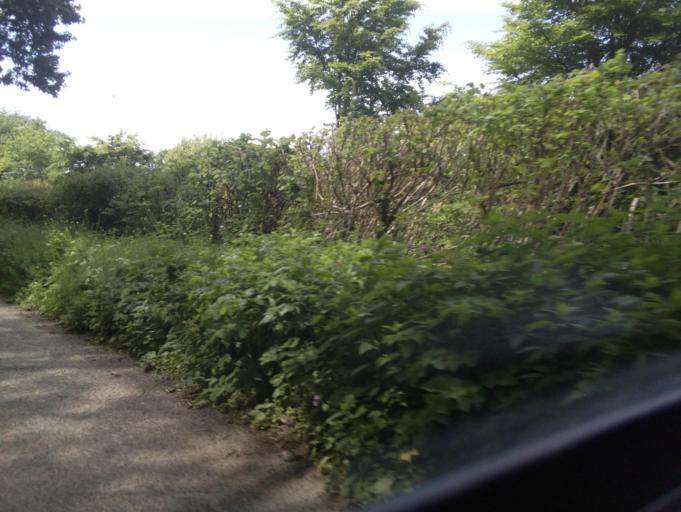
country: GB
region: England
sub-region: Devon
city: Kingsbridge
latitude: 50.3617
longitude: -3.7616
